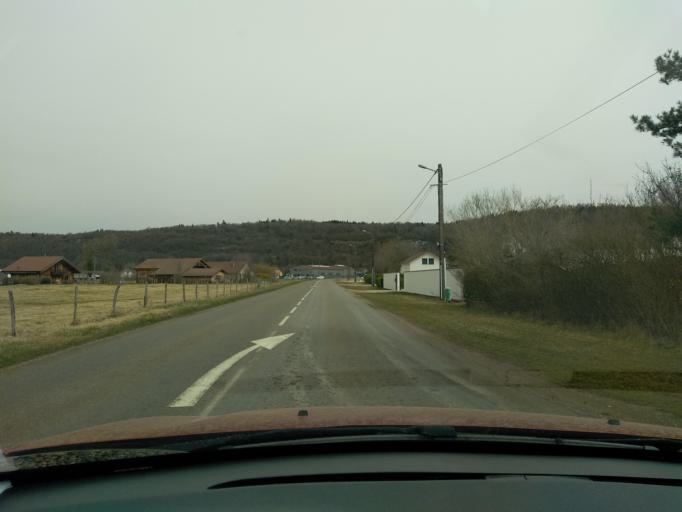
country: FR
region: Franche-Comte
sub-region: Departement du Jura
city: Clairvaux-les-Lacs
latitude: 46.6214
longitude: 5.7460
